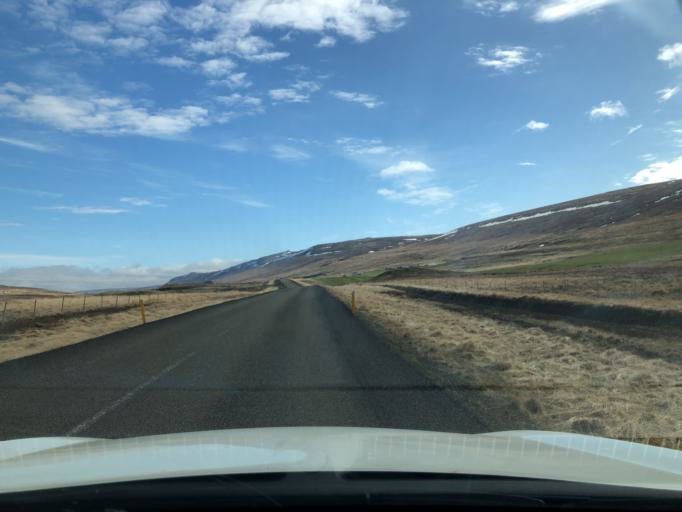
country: IS
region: West
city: Borgarnes
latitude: 65.1240
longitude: -21.6583
